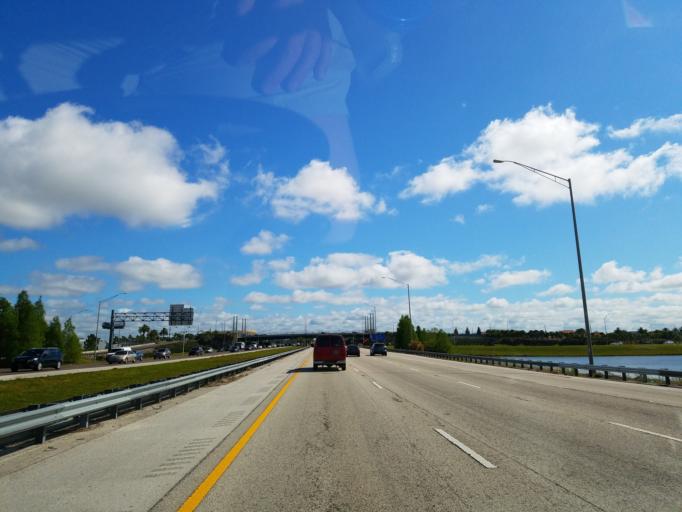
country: US
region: Florida
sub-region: Orange County
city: Oak Ridge
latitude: 28.4903
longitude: -81.4360
